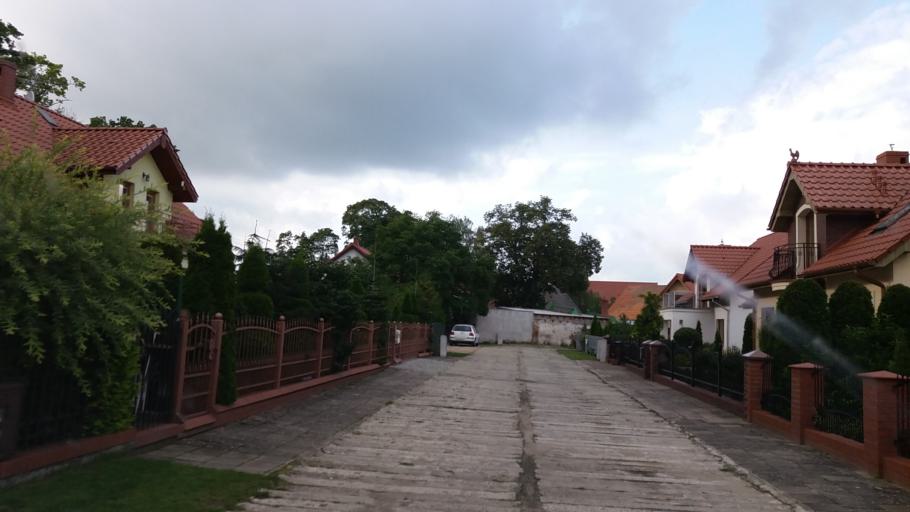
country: PL
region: West Pomeranian Voivodeship
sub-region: Powiat choszczenski
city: Choszczno
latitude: 53.1606
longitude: 15.4317
